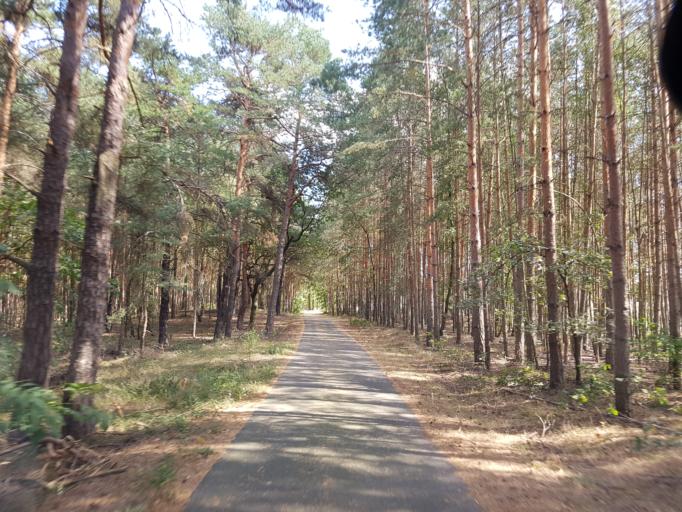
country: DE
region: Brandenburg
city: Finsterwalde
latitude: 51.6007
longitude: 13.7704
